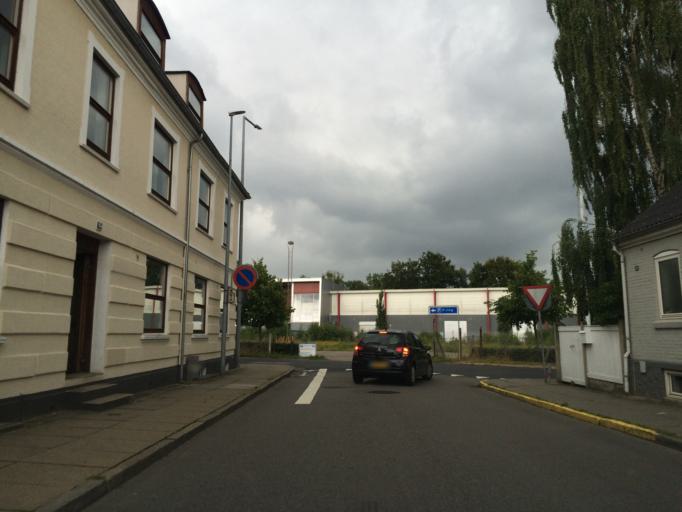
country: DK
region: Central Jutland
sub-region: Silkeborg Kommune
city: Silkeborg
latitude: 56.1645
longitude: 9.5376
